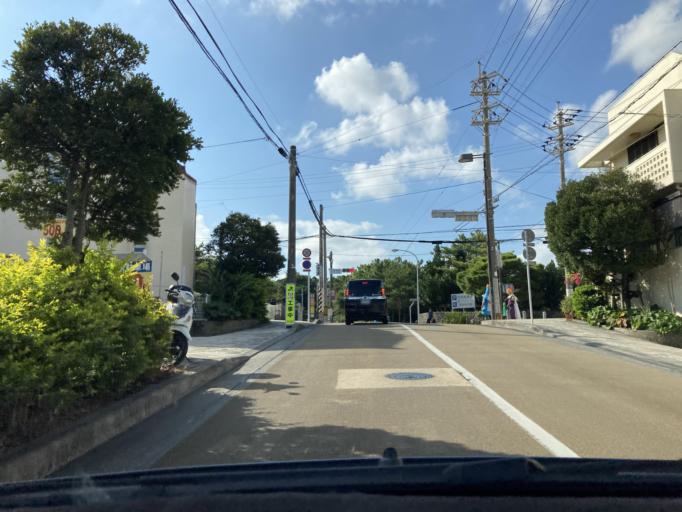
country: JP
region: Okinawa
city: Naha-shi
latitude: 26.2192
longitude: 127.7158
